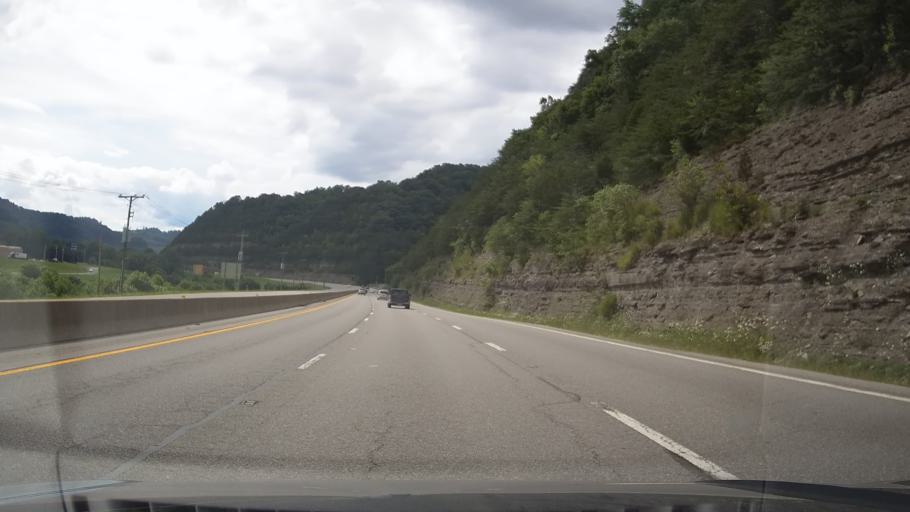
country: US
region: Kentucky
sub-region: Pike County
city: Coal Run Village
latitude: 37.5078
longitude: -82.5338
